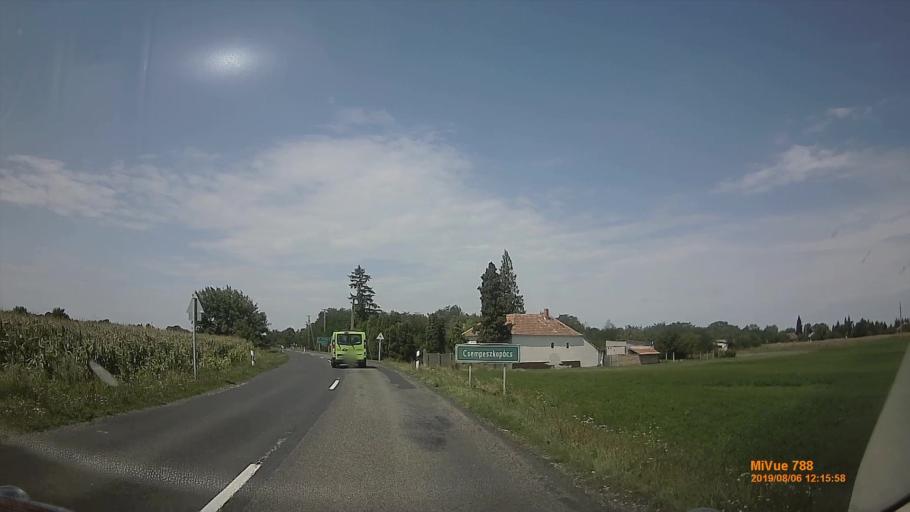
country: HU
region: Vas
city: Vasvar
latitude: 47.1521
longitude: 16.8102
